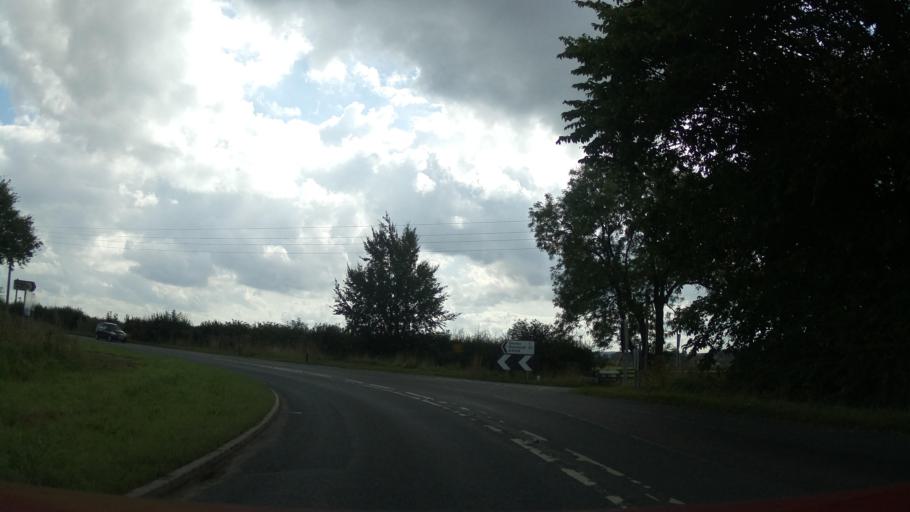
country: GB
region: England
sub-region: North Yorkshire
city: Catterick Garrison
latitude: 54.4256
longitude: -1.6834
